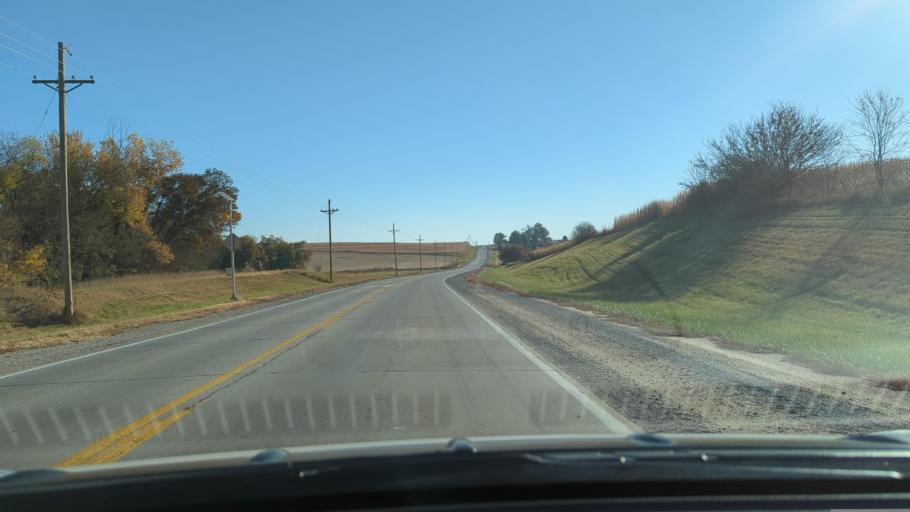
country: US
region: Nebraska
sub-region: Sarpy County
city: Papillion
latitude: 41.0923
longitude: -96.0406
